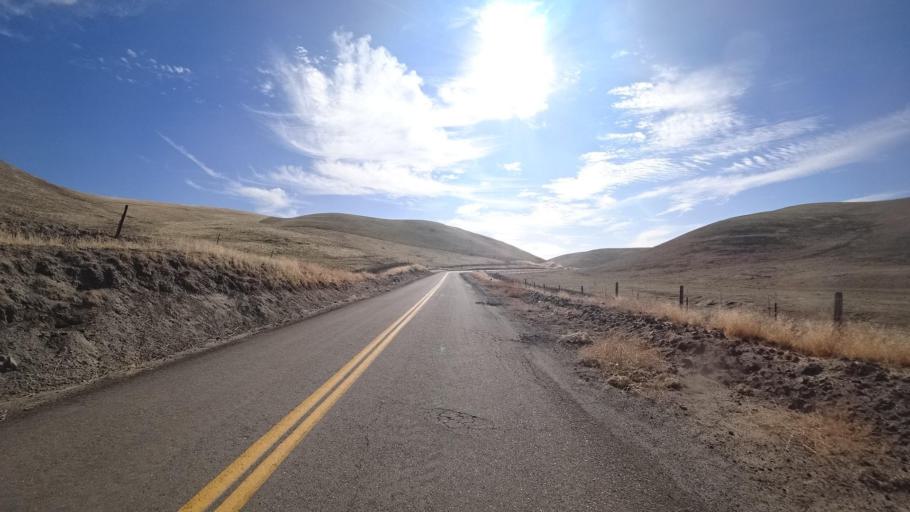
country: US
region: California
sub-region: Kern County
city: Oildale
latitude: 35.6189
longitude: -118.9420
